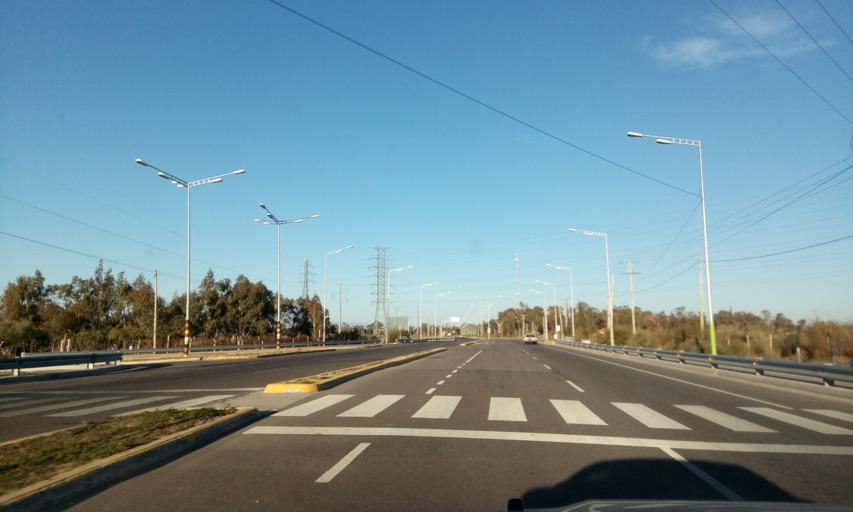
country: AR
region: San Juan
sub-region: Departamento de Rivadavia
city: Rivadavia
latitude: -31.5132
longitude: -68.6406
